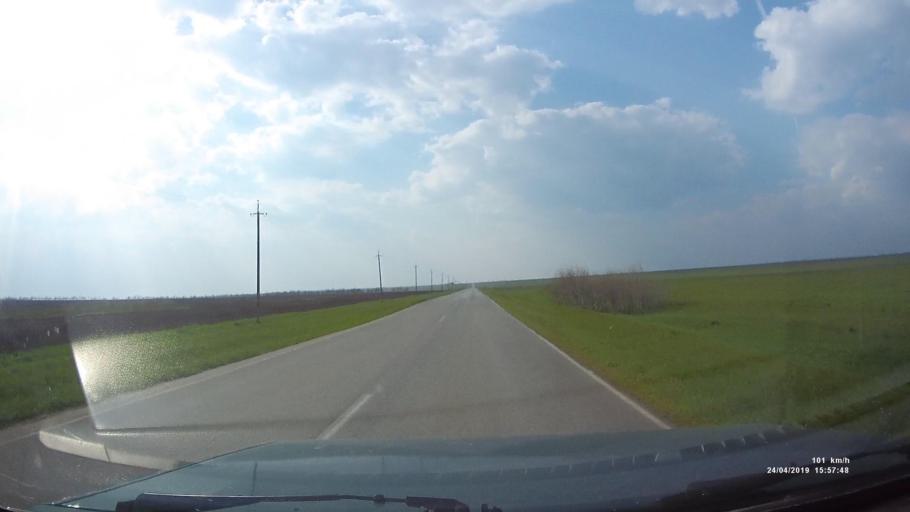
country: RU
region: Kalmykiya
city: Yashalta
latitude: 46.6081
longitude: 42.5021
